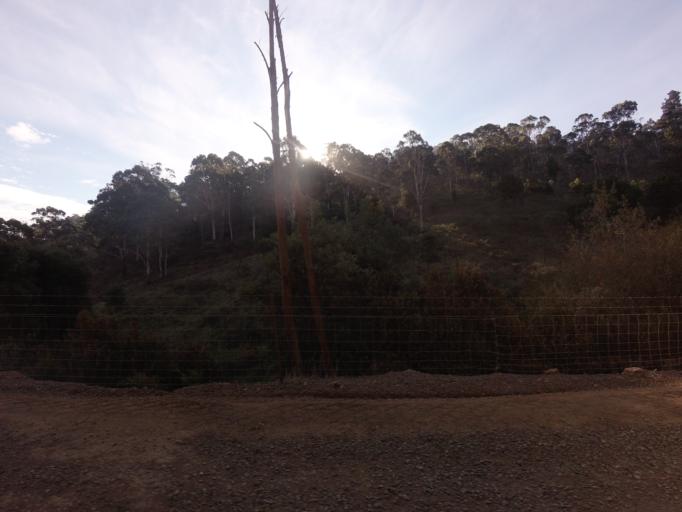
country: AU
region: Tasmania
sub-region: Brighton
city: Bridgewater
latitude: -42.5116
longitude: 147.4242
